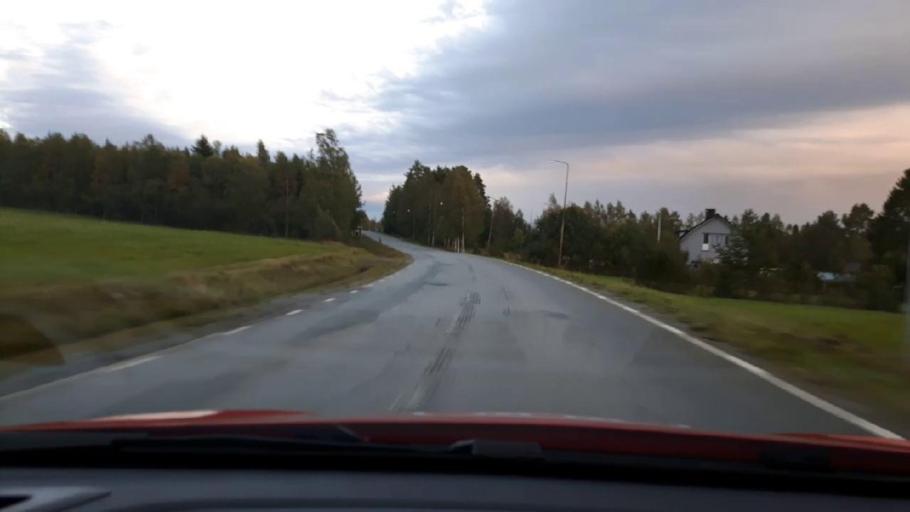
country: SE
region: Jaemtland
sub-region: Bergs Kommun
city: Hoverberg
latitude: 63.0226
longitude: 14.4780
